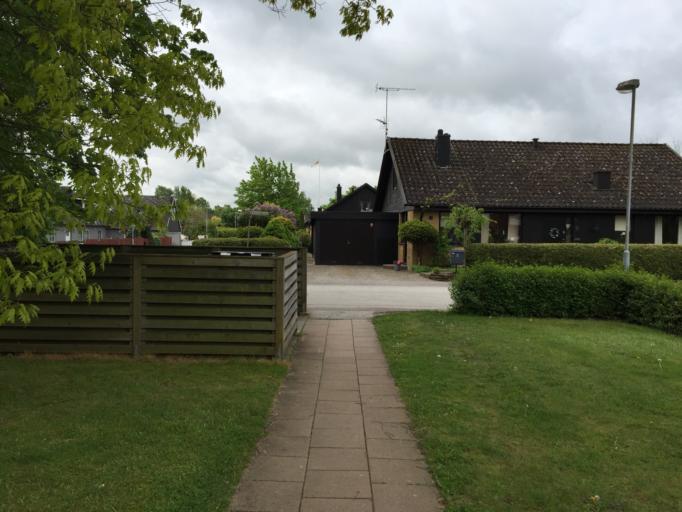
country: SE
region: Skane
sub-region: Lunds Kommun
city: Veberod
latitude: 55.6311
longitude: 13.4937
